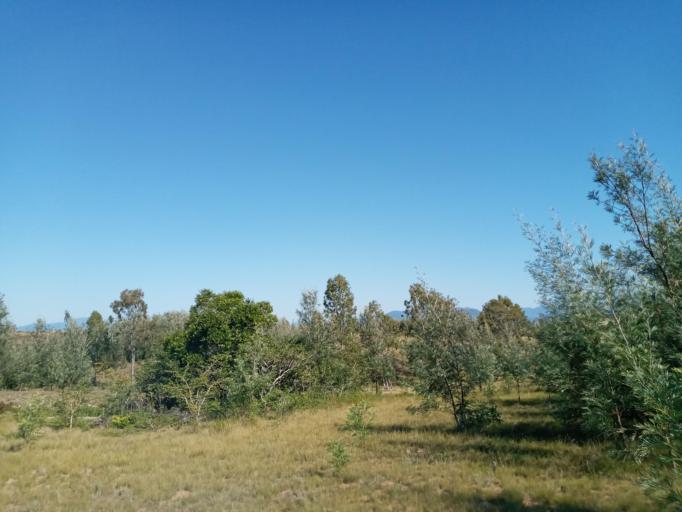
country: MG
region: Atsimo-Atsinanana
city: Vohipaho
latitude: -24.2455
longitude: 47.3153
